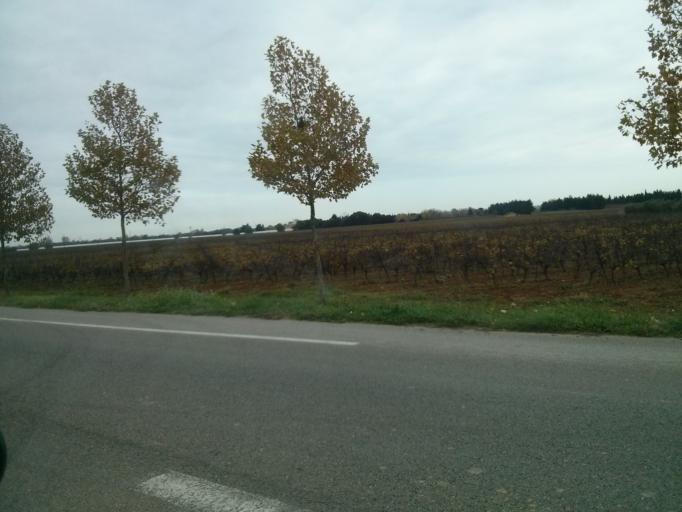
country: FR
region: Languedoc-Roussillon
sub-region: Departement du Gard
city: Mus
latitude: 43.7124
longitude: 4.1983
